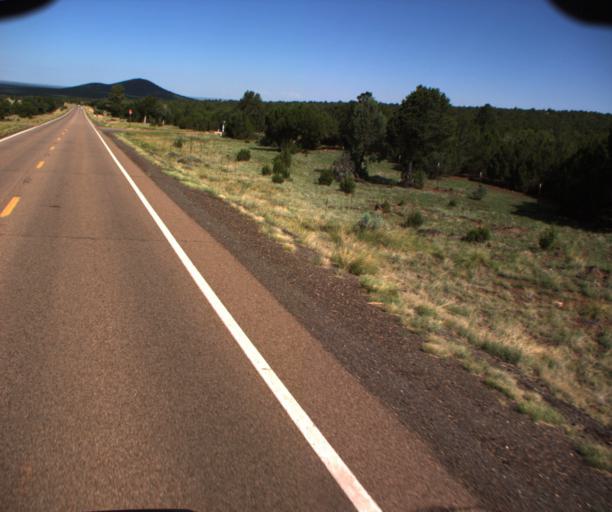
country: US
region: Arizona
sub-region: Navajo County
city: White Mountain Lake
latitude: 34.2829
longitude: -109.8128
